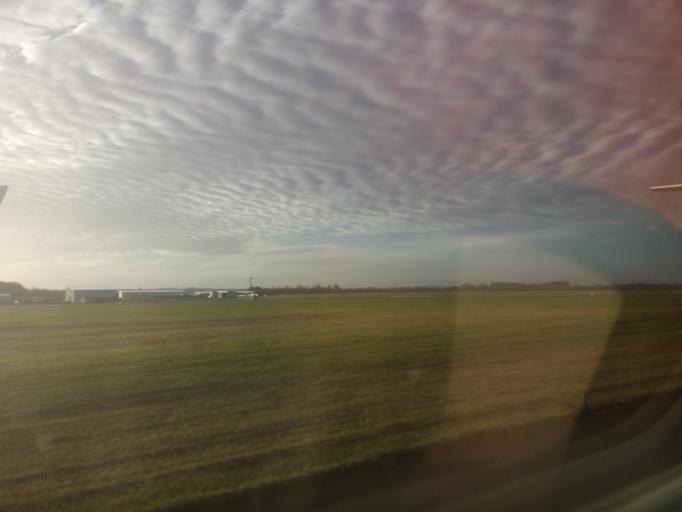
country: GB
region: England
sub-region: Newcastle upon Tyne
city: Dinnington
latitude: 55.0379
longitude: -1.6975
